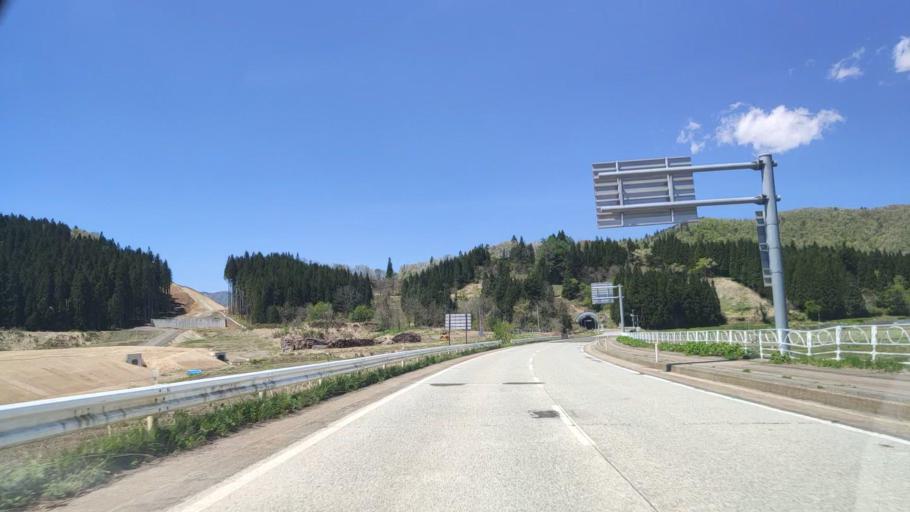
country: JP
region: Akita
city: Yuzawa
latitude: 39.0516
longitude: 140.4442
